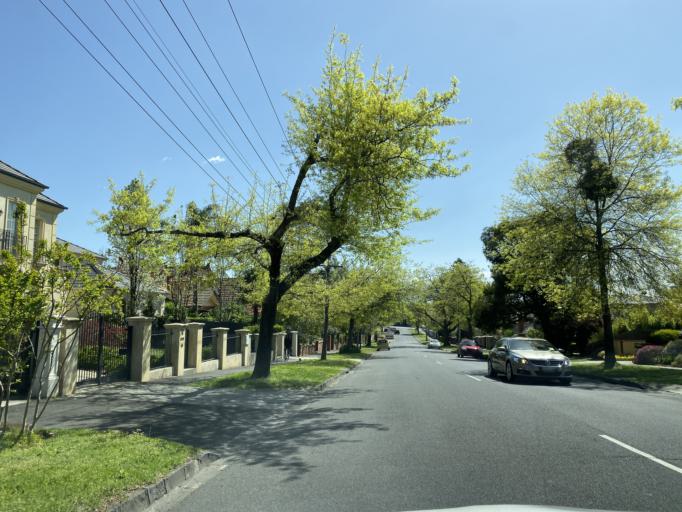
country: AU
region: Victoria
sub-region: Boroondara
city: Camberwell
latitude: -37.8449
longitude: 145.0690
